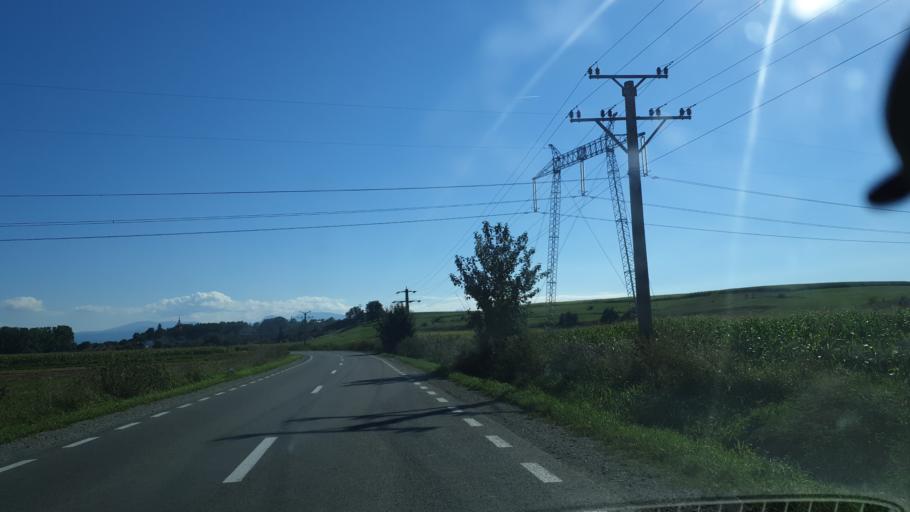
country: RO
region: Covasna
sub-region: Comuna Ilieni
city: Ilieni
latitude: 45.8085
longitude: 25.7720
